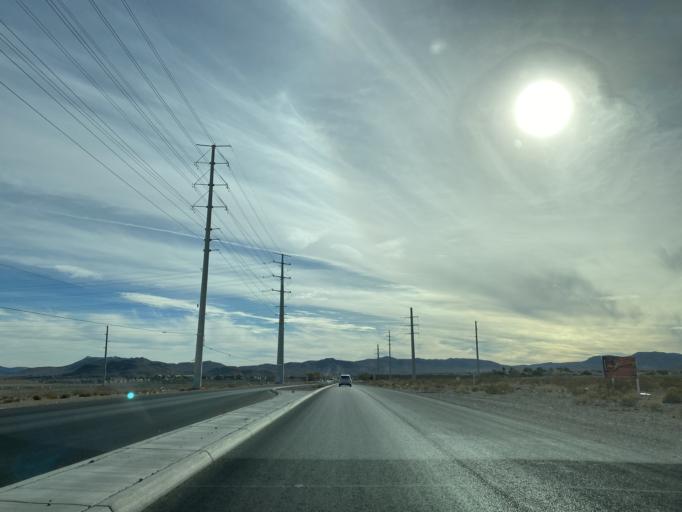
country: US
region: Nevada
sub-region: Clark County
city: Enterprise
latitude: 36.0112
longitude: -115.2436
